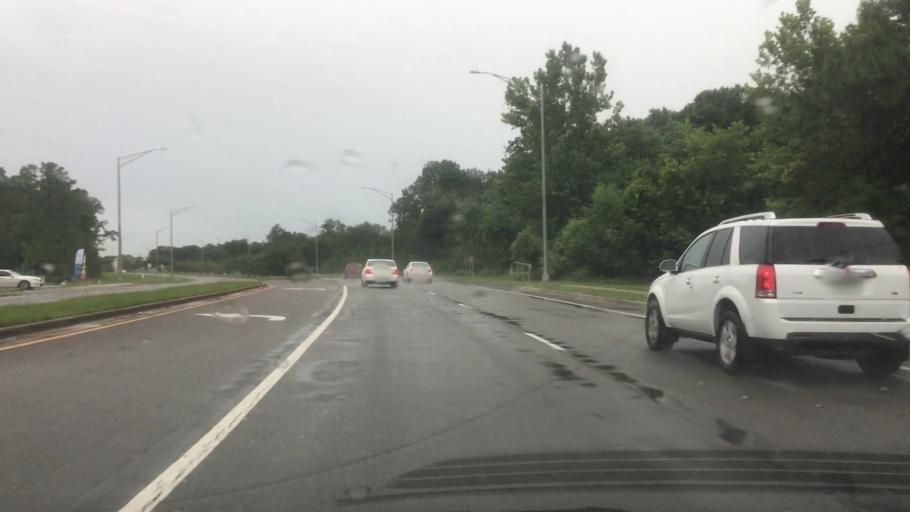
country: US
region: Florida
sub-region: Duval County
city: Jacksonville Beach
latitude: 30.2740
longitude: -81.5234
